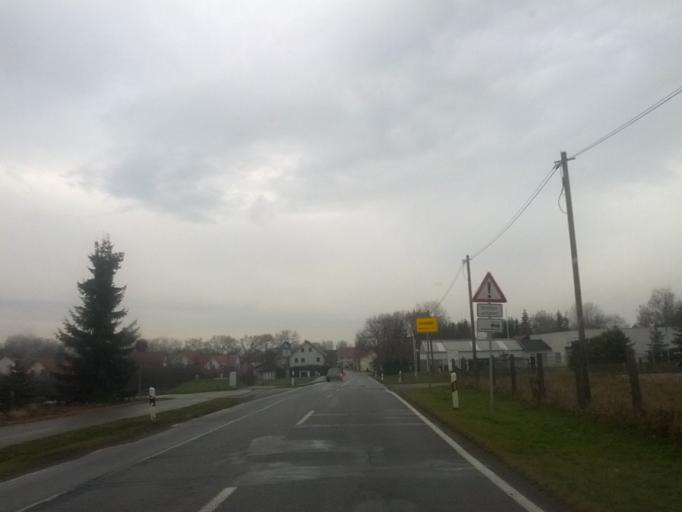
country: DE
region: Thuringia
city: Zimmernsupra
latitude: 50.9682
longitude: 10.8890
